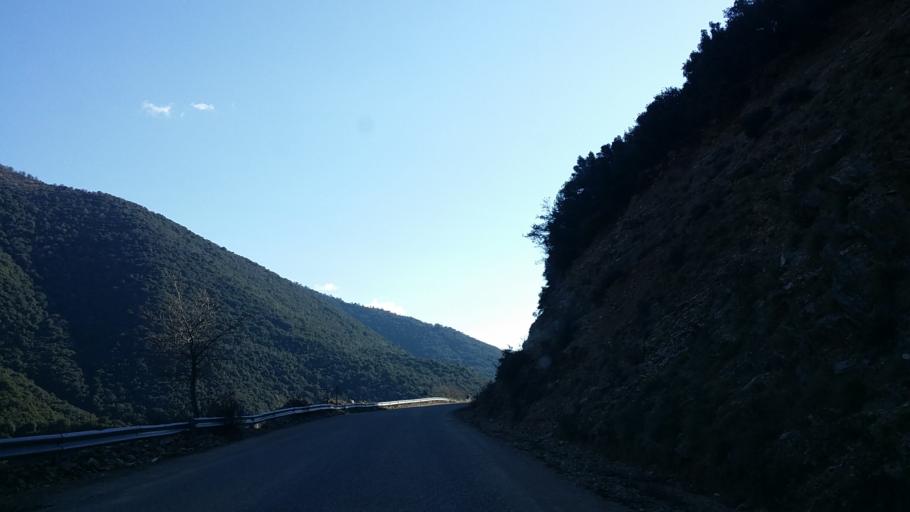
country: GR
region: Central Greece
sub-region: Nomos Evrytanias
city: Kerasochori
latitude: 38.9470
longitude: 21.6122
